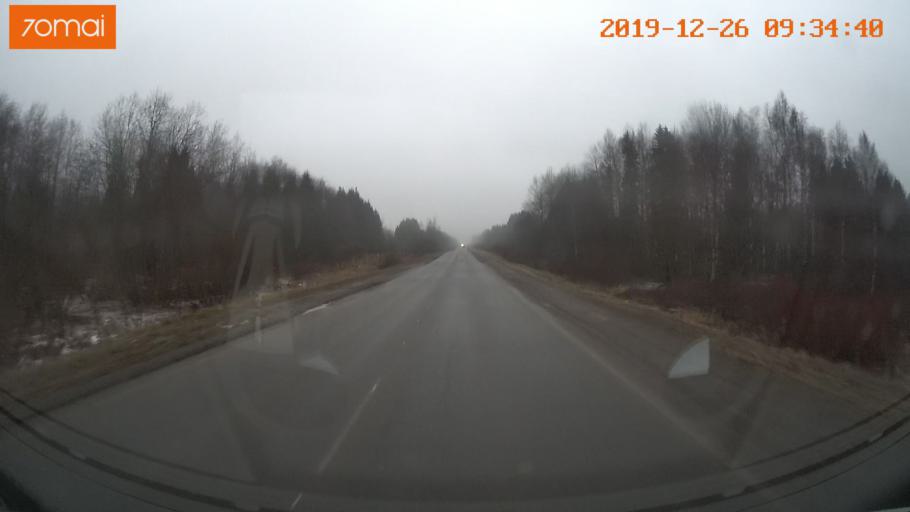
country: RU
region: Vologda
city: Vologda
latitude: 59.1043
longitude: 40.0832
